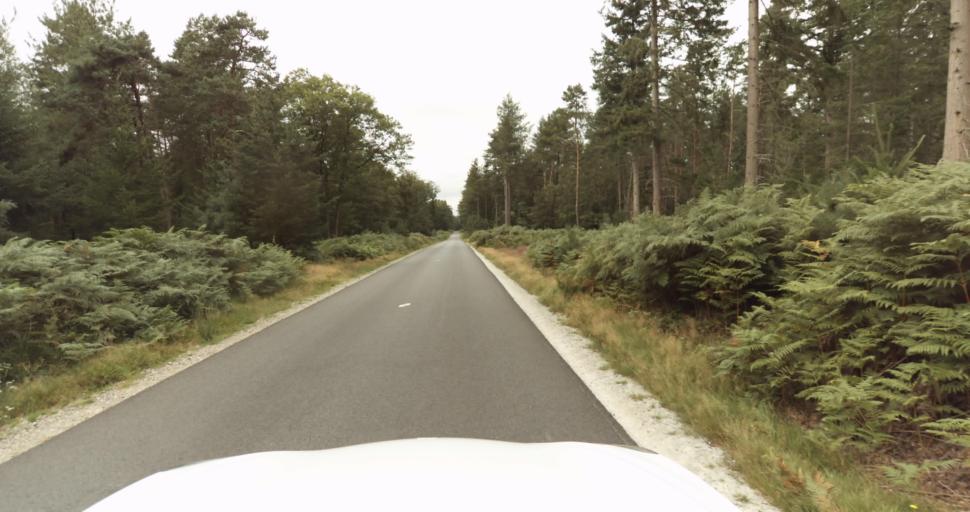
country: FR
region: Haute-Normandie
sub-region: Departement de l'Eure
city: Saint-Sebastien-de-Morsent
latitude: 48.9628
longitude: 1.0546
